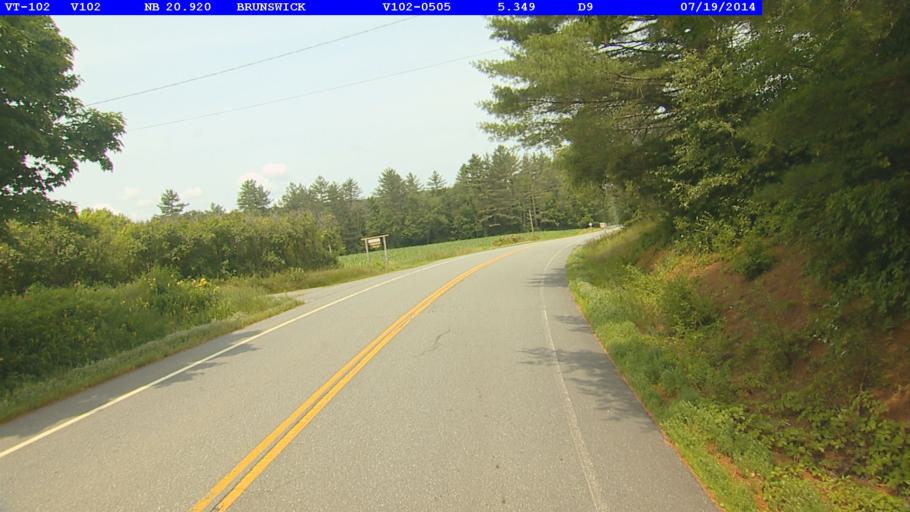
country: US
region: New Hampshire
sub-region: Coos County
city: Stratford
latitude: 44.7249
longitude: -71.6333
